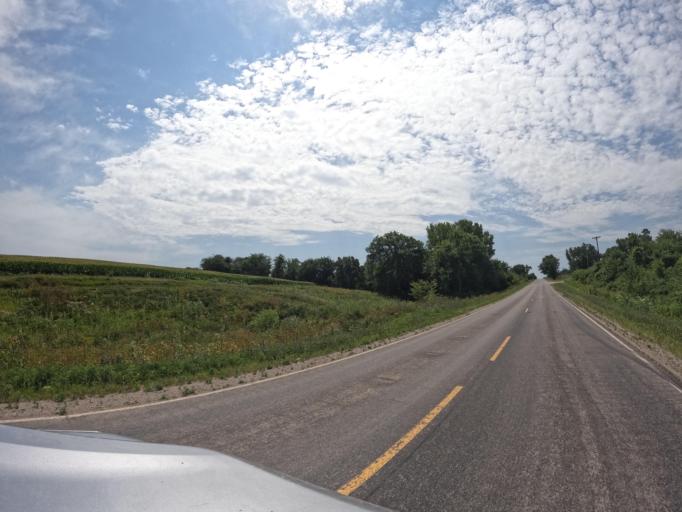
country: US
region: Iowa
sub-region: Appanoose County
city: Centerville
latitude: 40.7913
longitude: -92.9448
